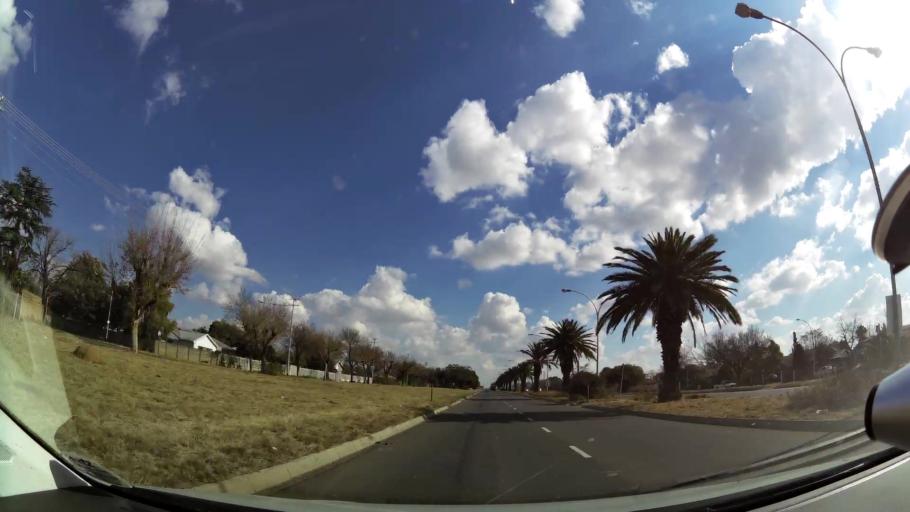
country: ZA
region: Orange Free State
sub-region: Mangaung Metropolitan Municipality
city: Bloemfontein
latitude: -29.1267
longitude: 26.1725
